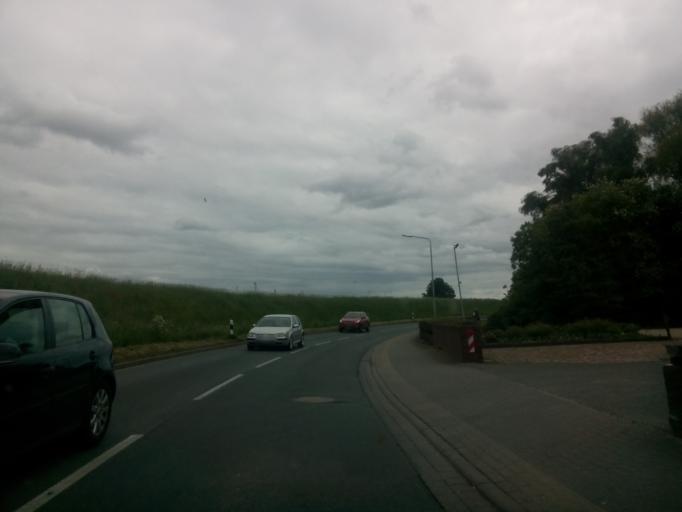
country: DE
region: Lower Saxony
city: Lemwerder
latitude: 53.1173
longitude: 8.6452
